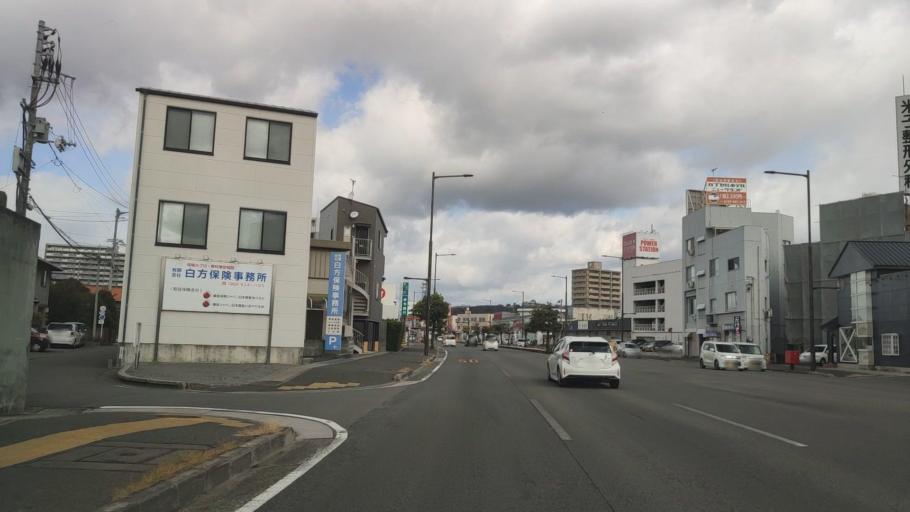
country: JP
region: Ehime
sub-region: Shikoku-chuo Shi
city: Matsuyama
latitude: 33.8260
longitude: 132.7586
